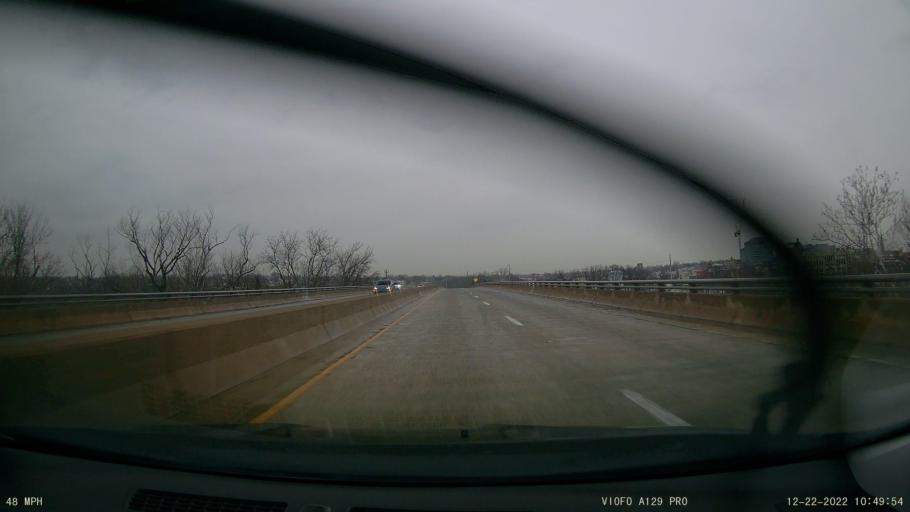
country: US
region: Pennsylvania
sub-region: Montgomery County
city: Bridgeport
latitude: 40.1108
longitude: -75.3506
